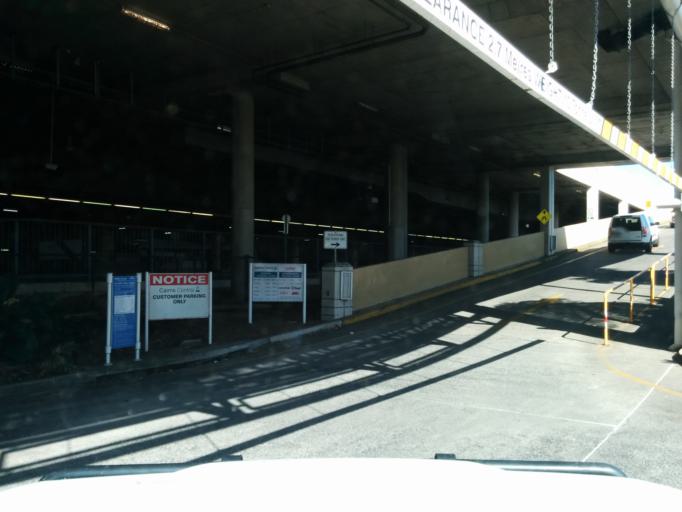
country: AU
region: Queensland
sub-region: Cairns
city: Cairns
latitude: -16.9249
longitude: 145.7702
